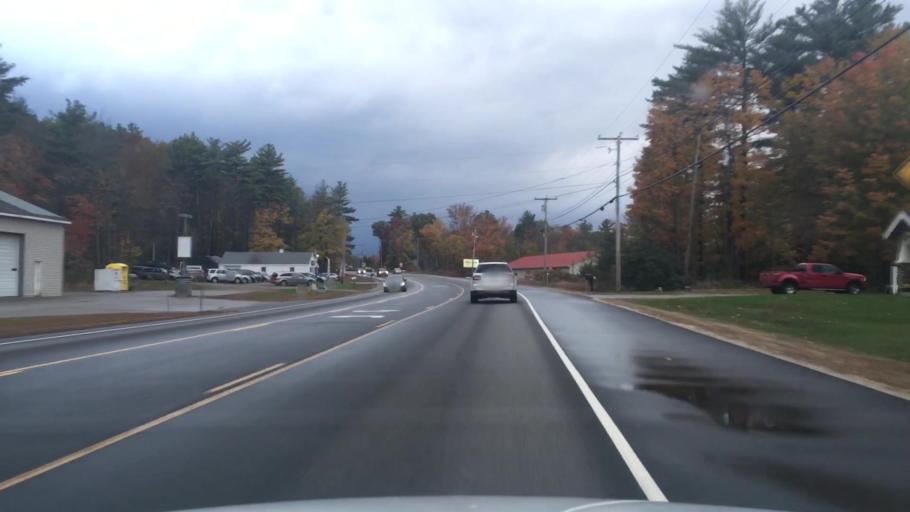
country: US
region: New Hampshire
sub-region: Merrimack County
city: Chichester
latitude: 43.2468
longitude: -71.4105
